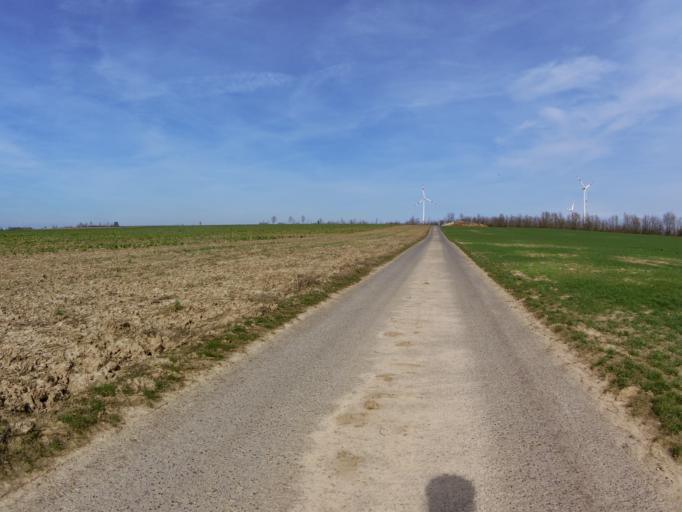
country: DE
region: Bavaria
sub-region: Regierungsbezirk Unterfranken
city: Biebelried
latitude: 49.7586
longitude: 10.1011
